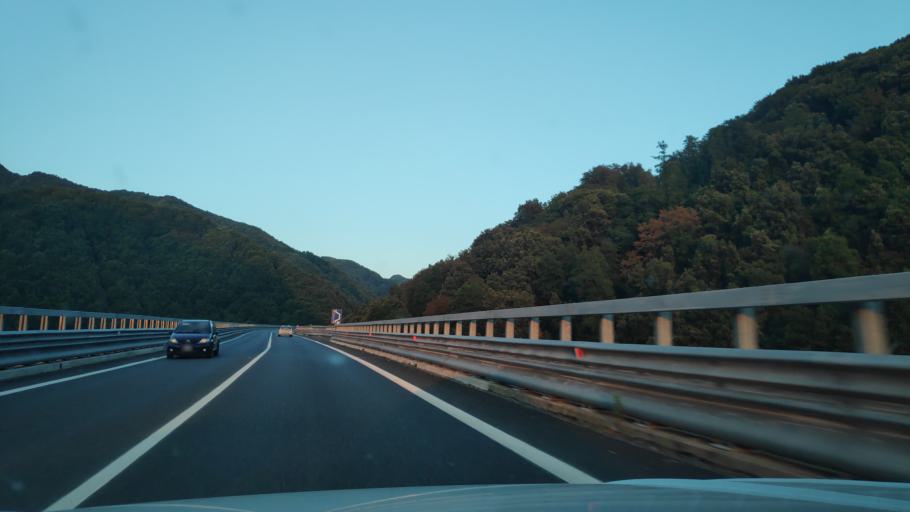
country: IT
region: Calabria
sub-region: Provincia di Reggio Calabria
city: Giffone
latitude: 38.4138
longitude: 16.1332
